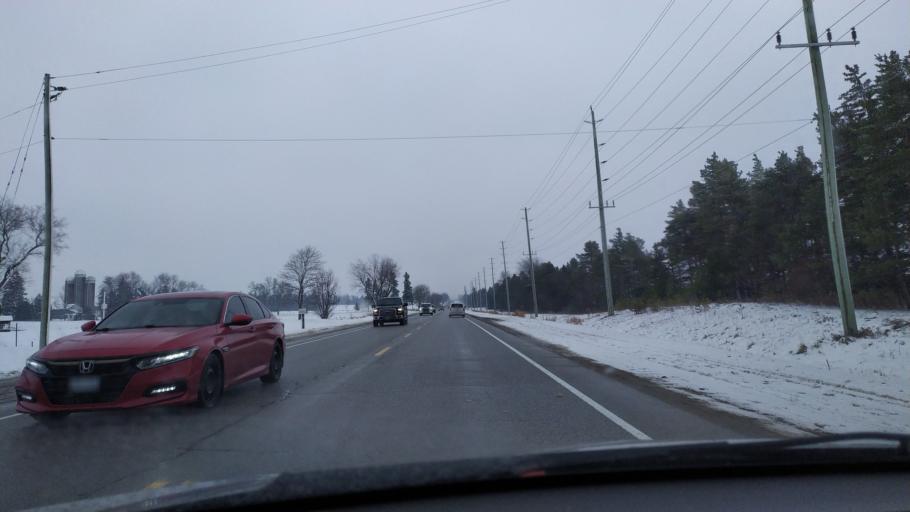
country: CA
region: Ontario
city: Waterloo
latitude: 43.6181
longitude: -80.6805
